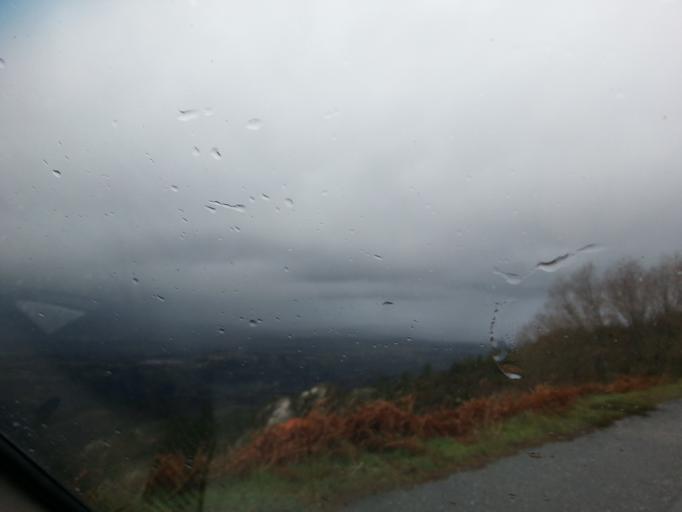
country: PT
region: Guarda
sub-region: Celorico da Beira
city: Celorico da Beira
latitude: 40.5237
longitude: -7.4532
